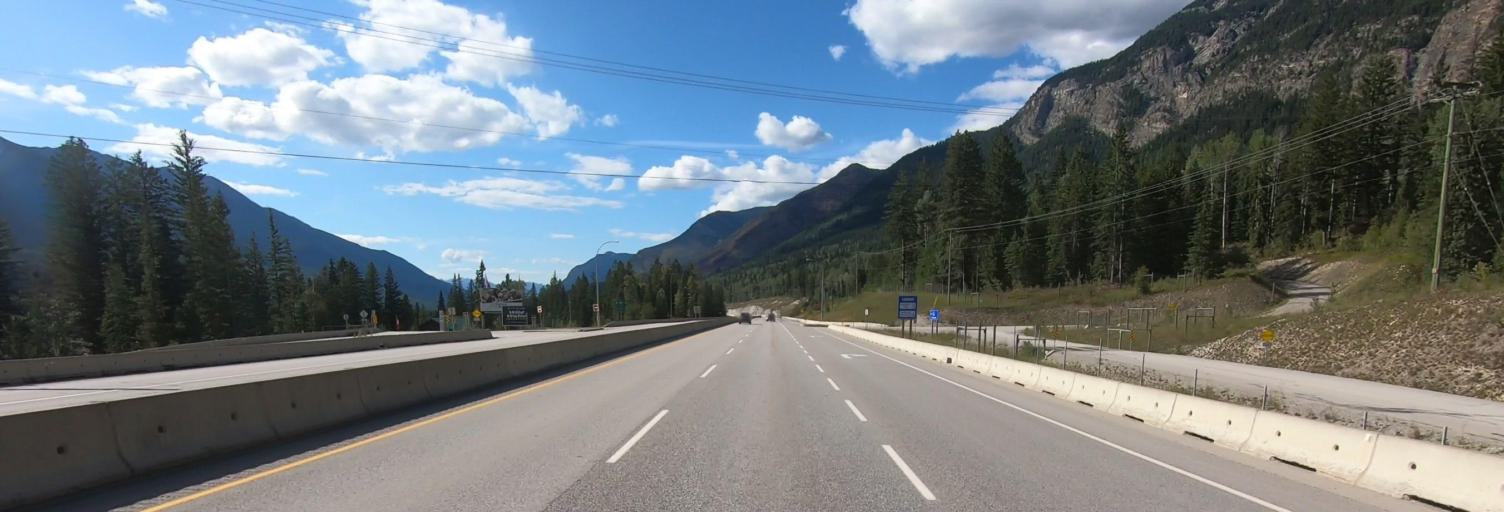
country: CA
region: British Columbia
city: Golden
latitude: 51.2423
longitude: -116.6579
